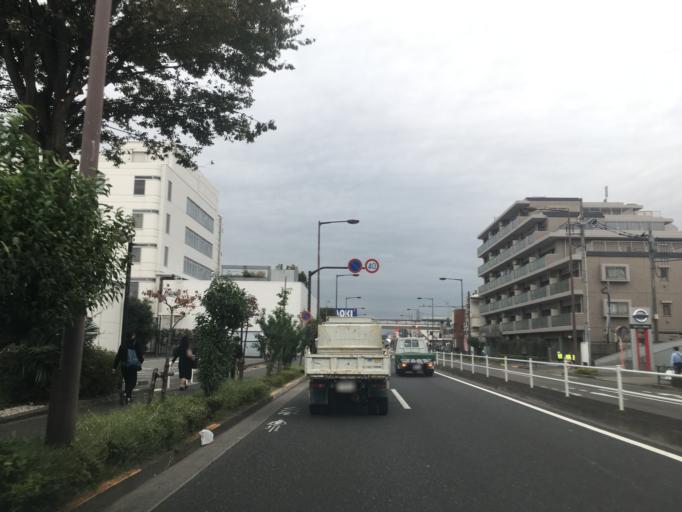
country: JP
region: Tokyo
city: Higashimurayama-shi
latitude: 35.7363
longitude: 139.4658
